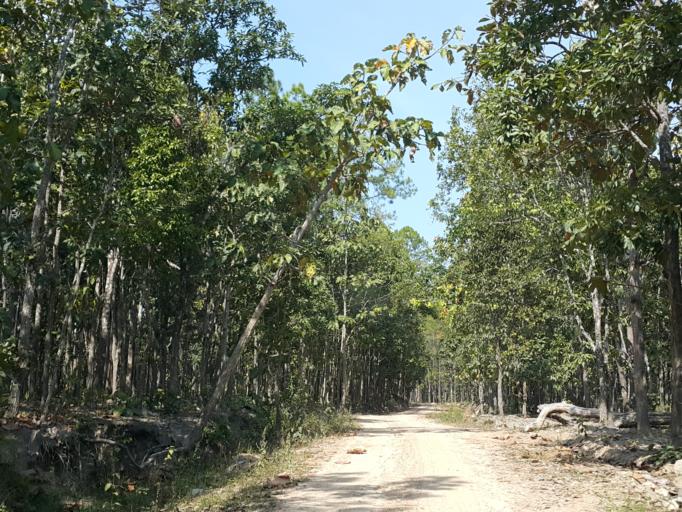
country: TH
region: Chiang Mai
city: Hot
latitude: 18.1508
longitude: 98.4308
